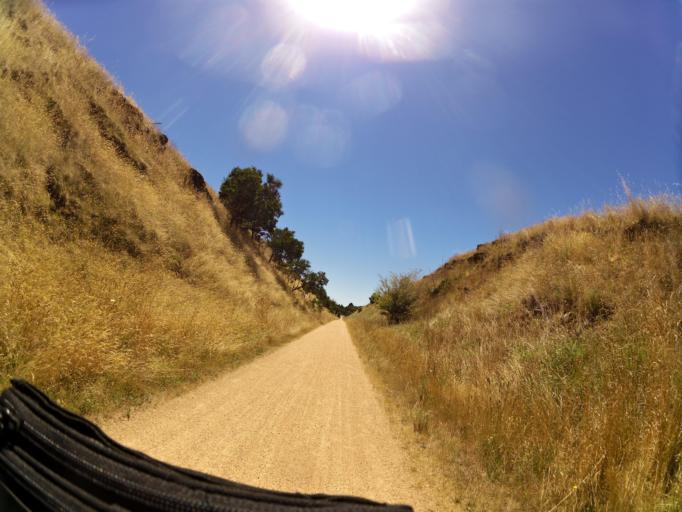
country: AU
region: Victoria
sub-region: Ballarat North
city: Delacombe
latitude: -37.7042
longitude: 143.6347
